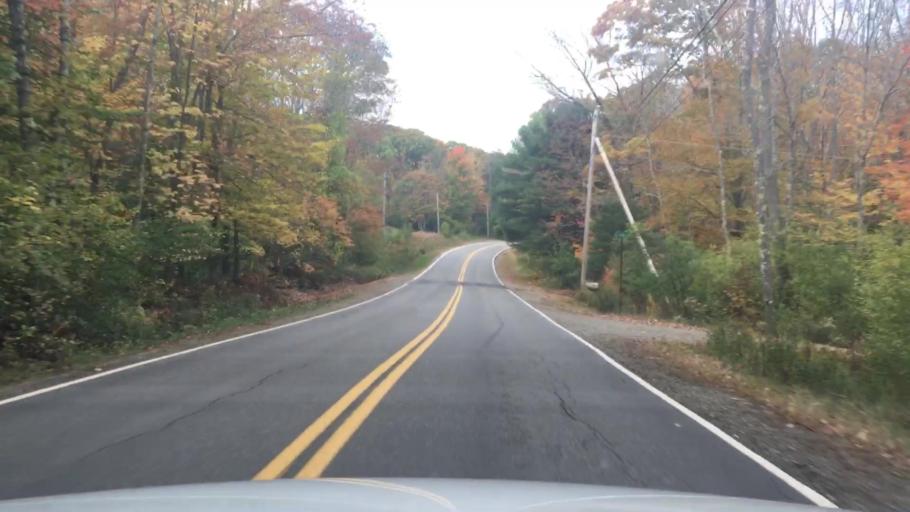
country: US
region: Maine
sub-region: Knox County
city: Hope
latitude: 44.2422
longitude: -69.1175
